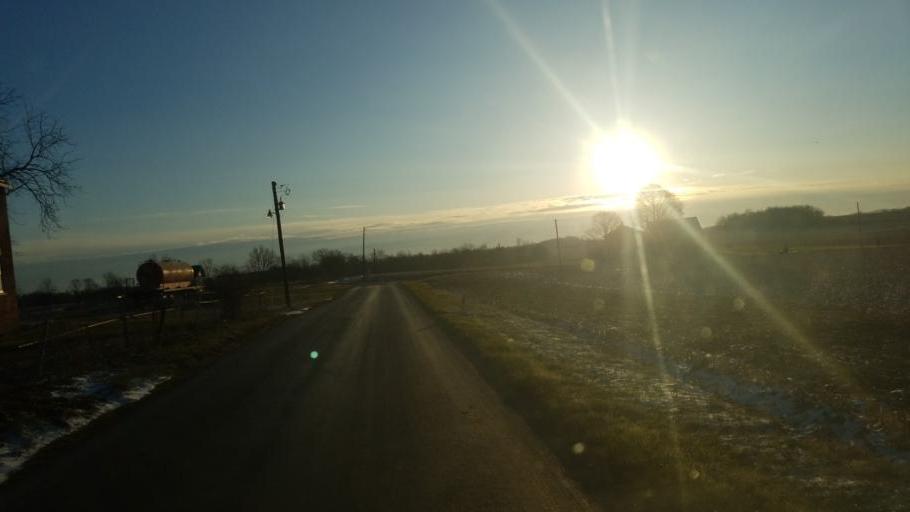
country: US
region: Ohio
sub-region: Highland County
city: Leesburg
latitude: 39.2564
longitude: -83.5051
